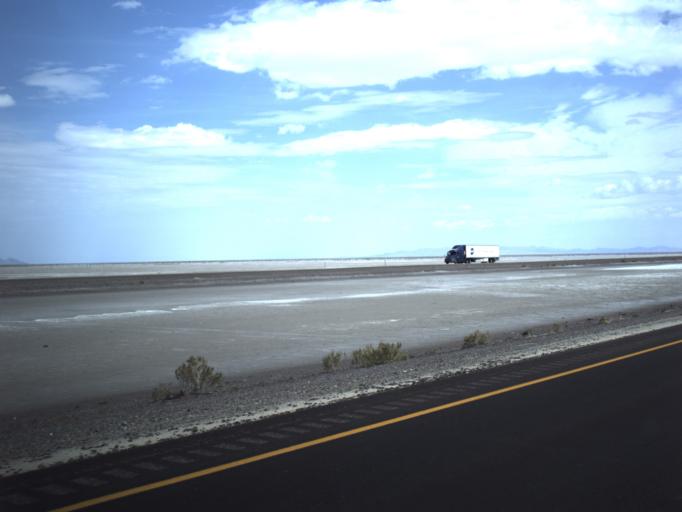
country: US
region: Utah
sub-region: Tooele County
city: Wendover
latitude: 40.7332
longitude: -113.6003
